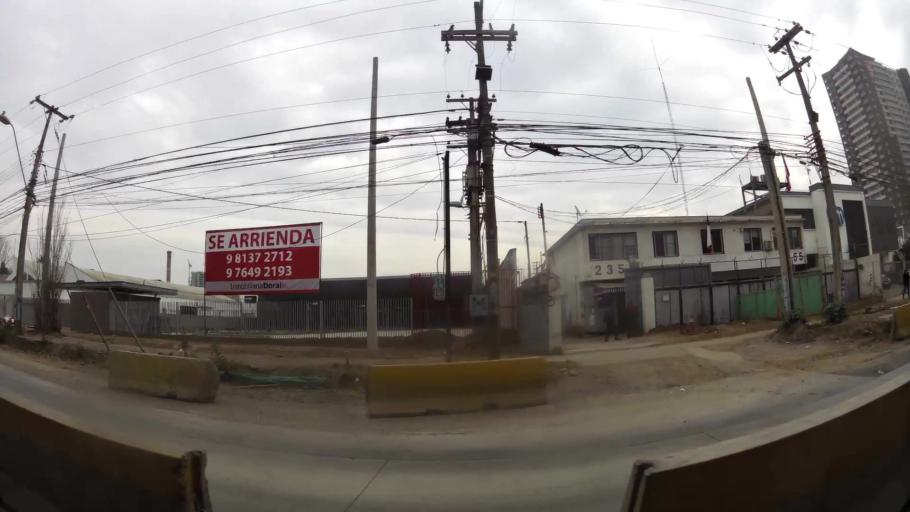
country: CL
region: Santiago Metropolitan
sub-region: Provincia de Santiago
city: Santiago
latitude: -33.4728
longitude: -70.6237
